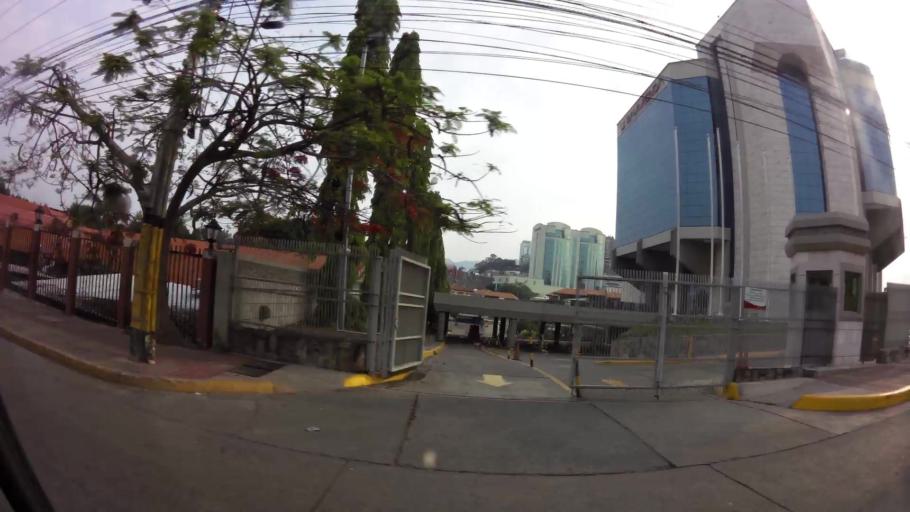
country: HN
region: Francisco Morazan
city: Tegucigalpa
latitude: 14.0865
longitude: -87.1914
